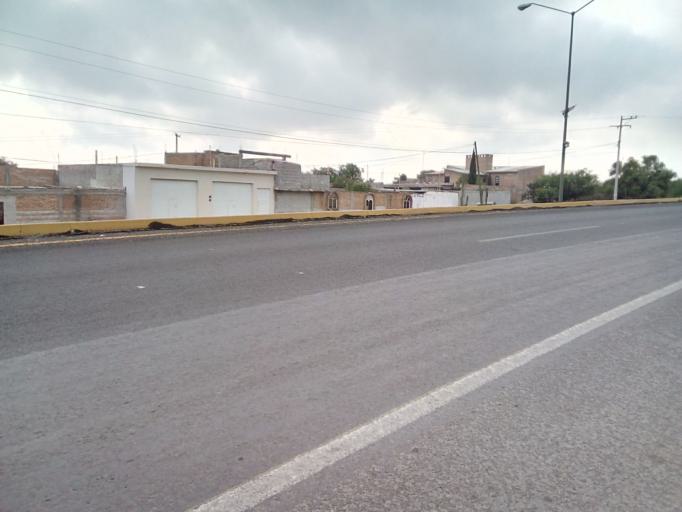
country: MX
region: Guerrero
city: San Luis de la Paz
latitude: 21.2807
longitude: -100.5020
